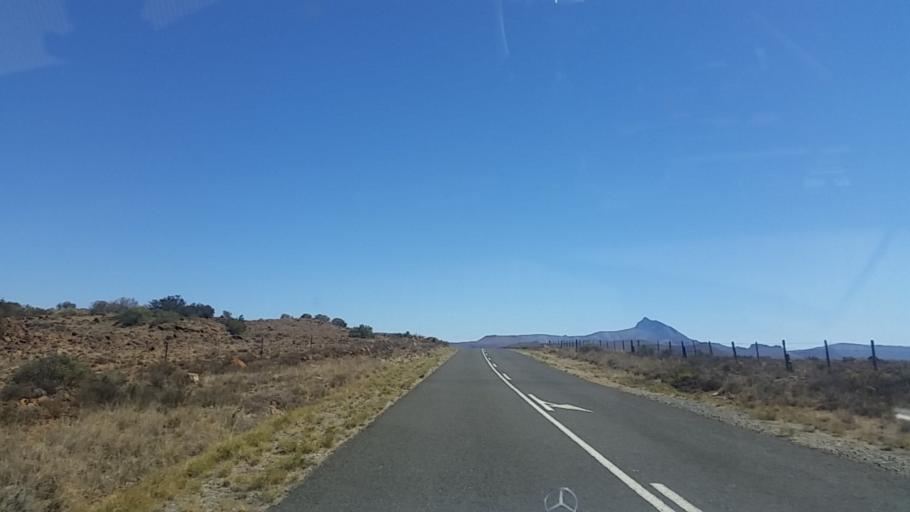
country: ZA
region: Eastern Cape
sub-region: Cacadu District Municipality
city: Graaff-Reinet
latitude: -31.9020
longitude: 24.5901
